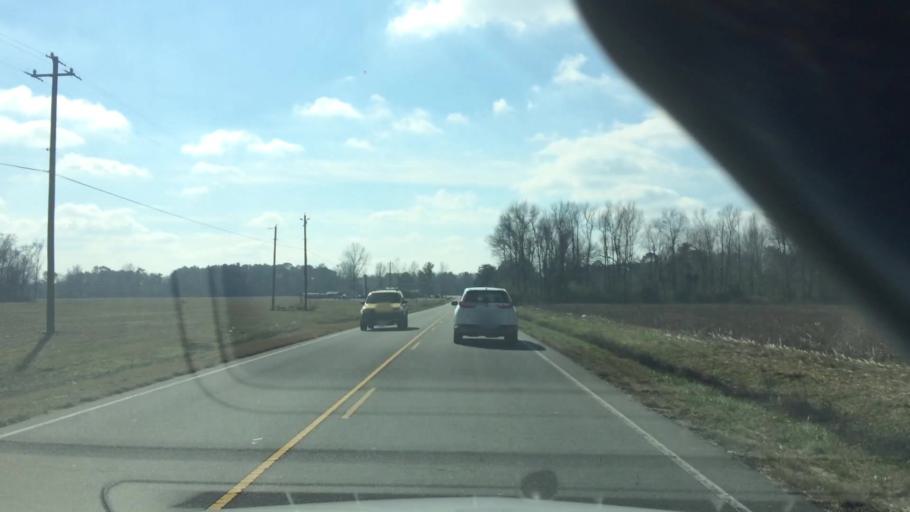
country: US
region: North Carolina
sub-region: Duplin County
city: Beulaville
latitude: 34.8858
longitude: -77.7857
